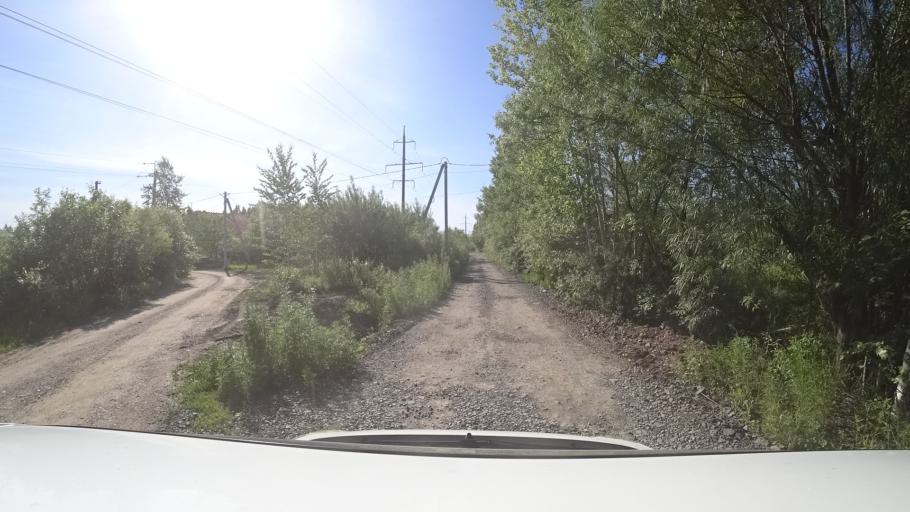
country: RU
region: Khabarovsk Krai
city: Topolevo
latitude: 48.5414
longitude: 135.1719
